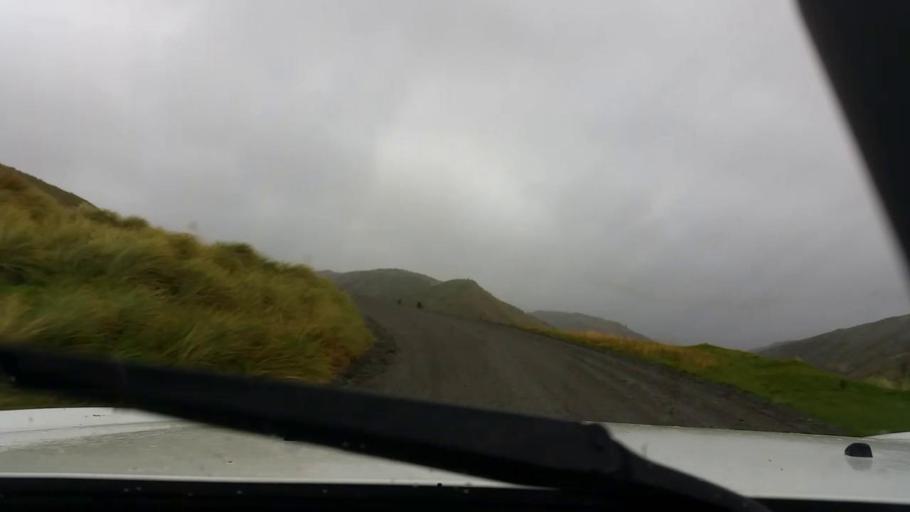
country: NZ
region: Wellington
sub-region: Masterton District
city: Masterton
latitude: -41.2511
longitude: 175.9151
